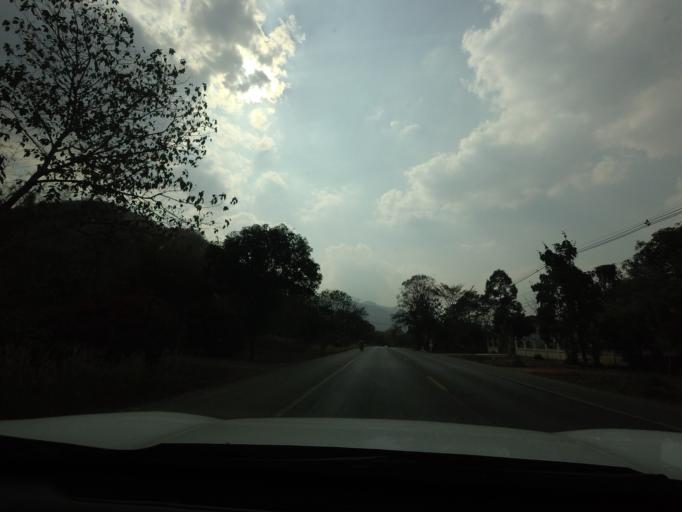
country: TH
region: Nakhon Ratchasima
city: Pak Chong
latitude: 14.5170
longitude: 101.3895
